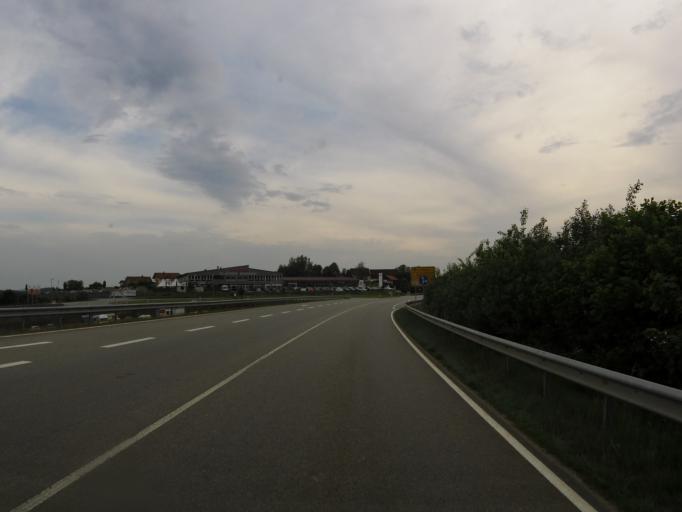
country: DE
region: Bavaria
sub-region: Lower Bavaria
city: Hutthurm
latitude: 48.6688
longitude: 13.4855
